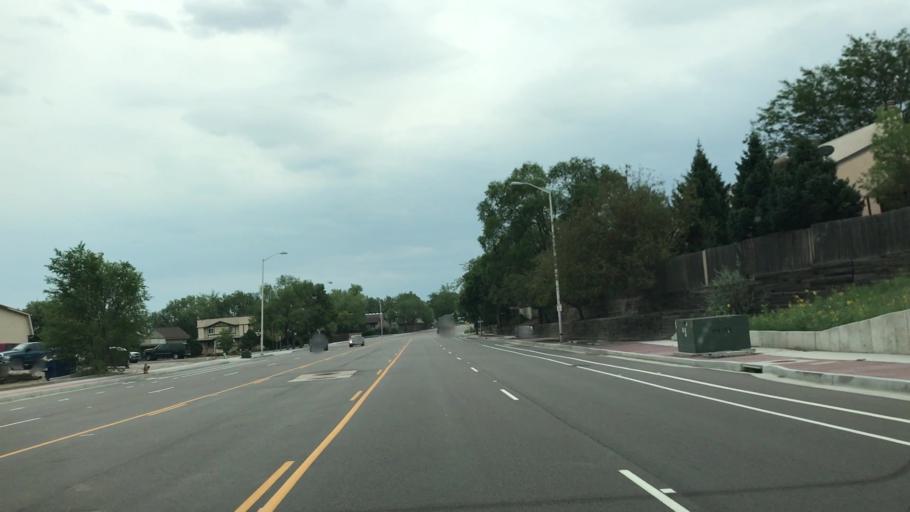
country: US
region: Colorado
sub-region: El Paso County
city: Colorado Springs
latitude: 38.8896
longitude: -104.8484
